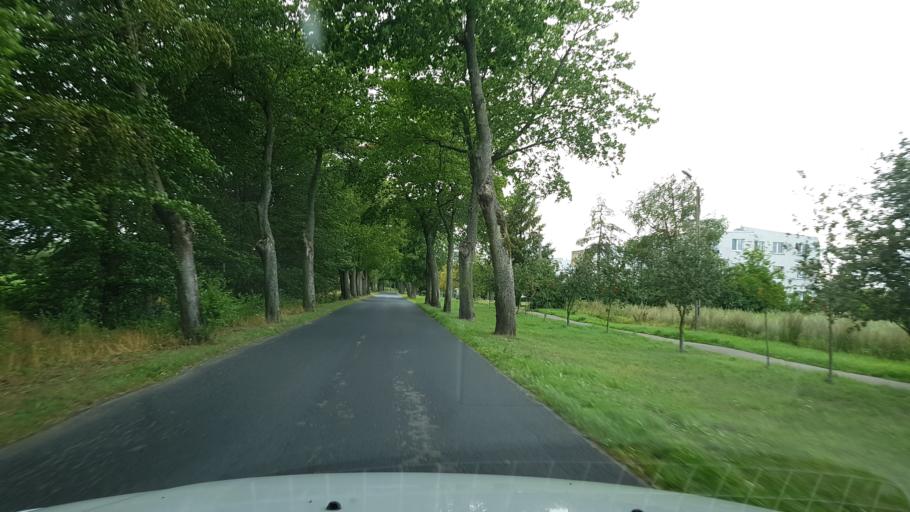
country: PL
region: West Pomeranian Voivodeship
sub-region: Powiat bialogardzki
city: Karlino
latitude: 54.1156
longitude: 15.8276
